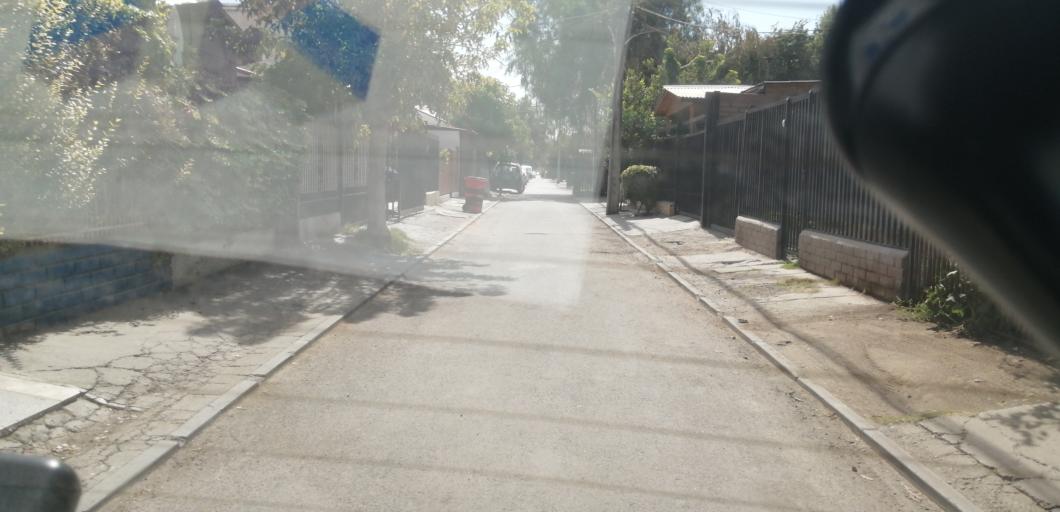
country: CL
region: Santiago Metropolitan
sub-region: Provincia de Santiago
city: Lo Prado
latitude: -33.4665
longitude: -70.7438
